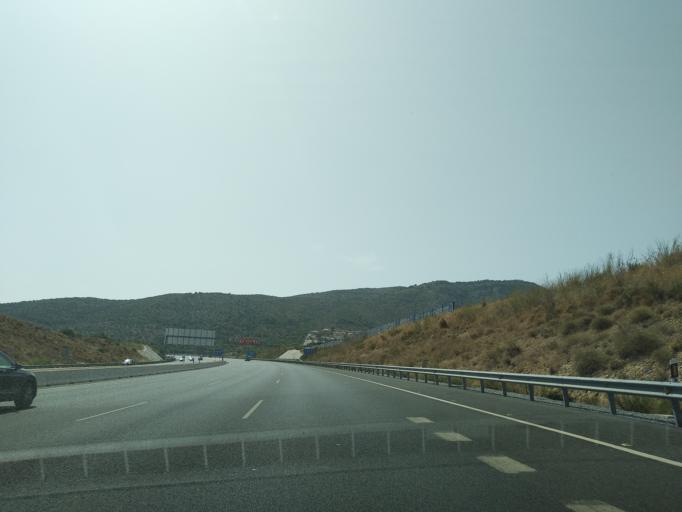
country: ES
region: Andalusia
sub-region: Provincia de Malaga
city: Alhaurin de la Torre
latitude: 36.6679
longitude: -4.5295
